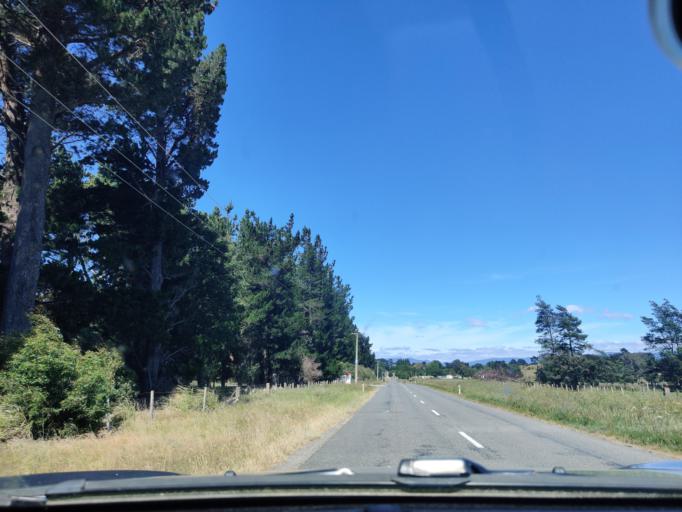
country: NZ
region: Wellington
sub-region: South Wairarapa District
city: Waipawa
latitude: -41.2255
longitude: 175.3497
